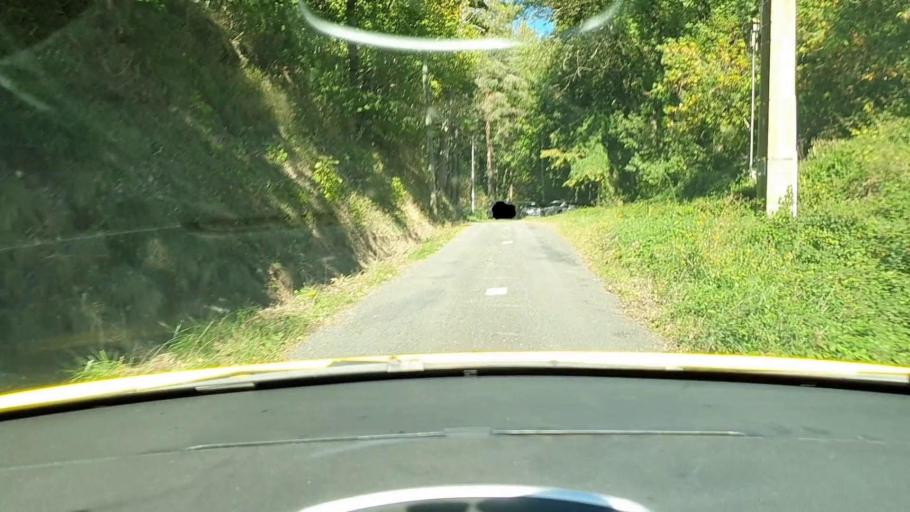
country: FR
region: Languedoc-Roussillon
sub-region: Departement du Gard
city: Le Vigan
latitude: 43.9936
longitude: 3.4577
